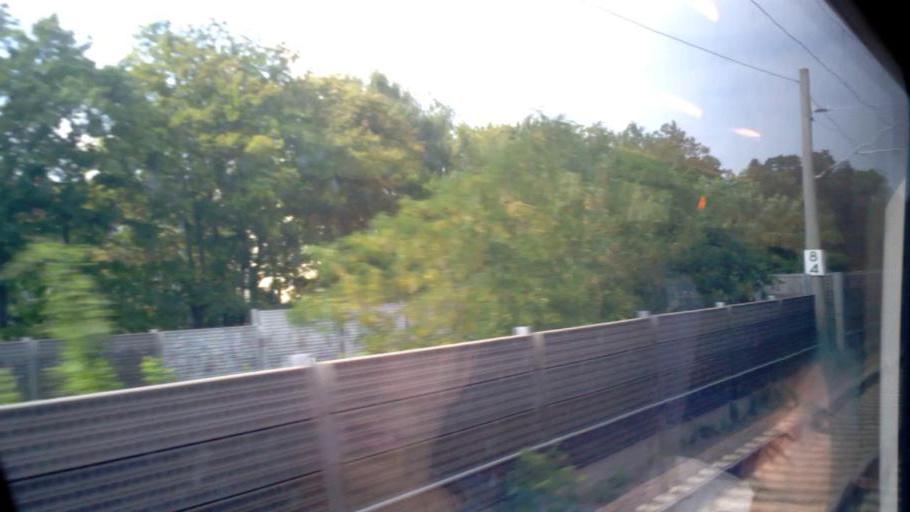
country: DE
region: Berlin
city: Lankwitz
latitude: 52.4343
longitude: 13.3358
